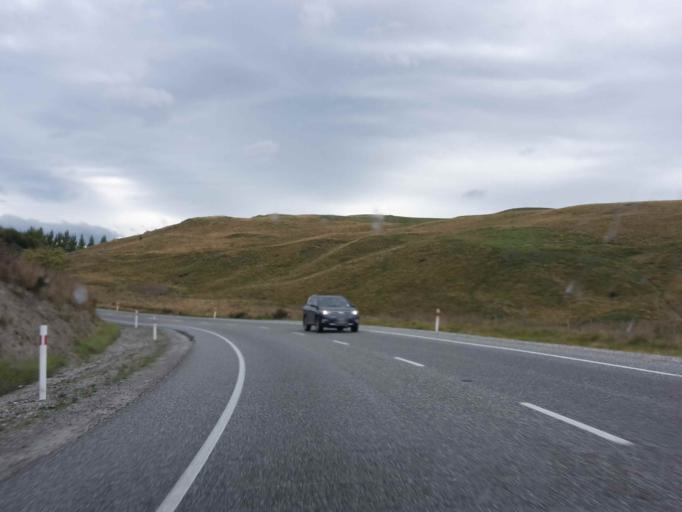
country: NZ
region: Otago
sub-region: Queenstown-Lakes District
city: Arrowtown
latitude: -44.9793
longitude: 168.8334
